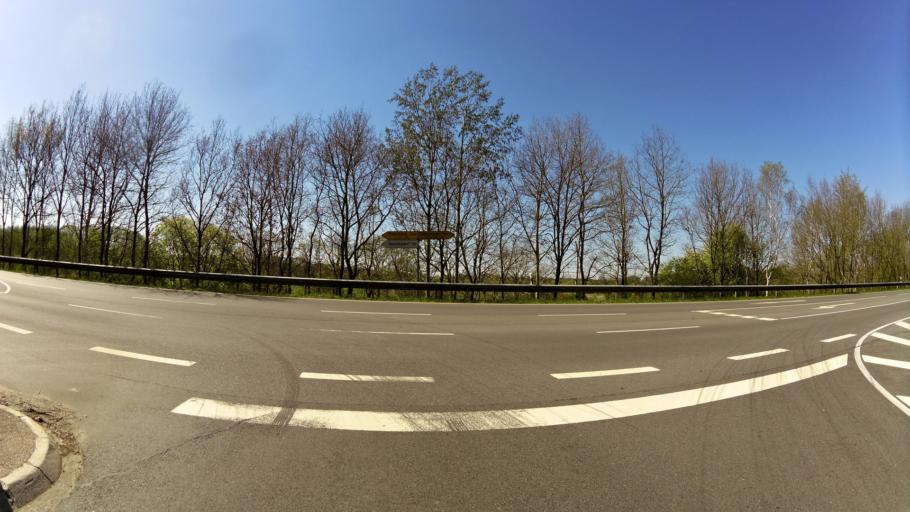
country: DE
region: Lower Saxony
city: Rotenburg
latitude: 53.1283
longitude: 9.4232
